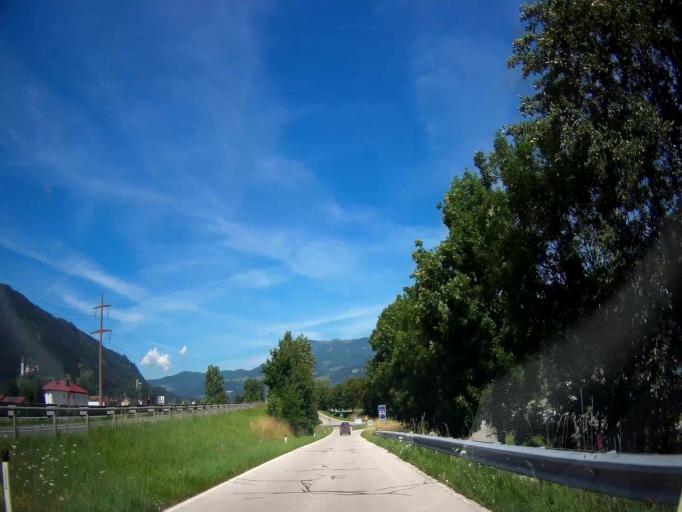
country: AT
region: Carinthia
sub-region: Politischer Bezirk Sankt Veit an der Glan
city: Friesach
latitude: 46.9512
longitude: 14.4216
